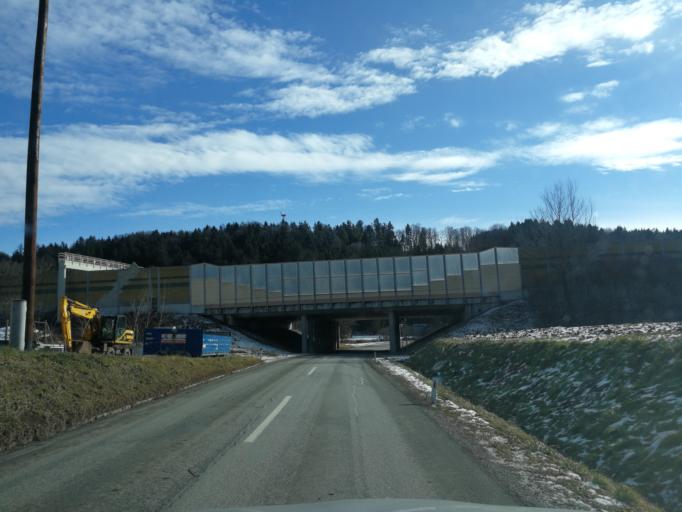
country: AT
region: Styria
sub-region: Politischer Bezirk Weiz
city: Ungerdorf
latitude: 47.0816
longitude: 15.6468
